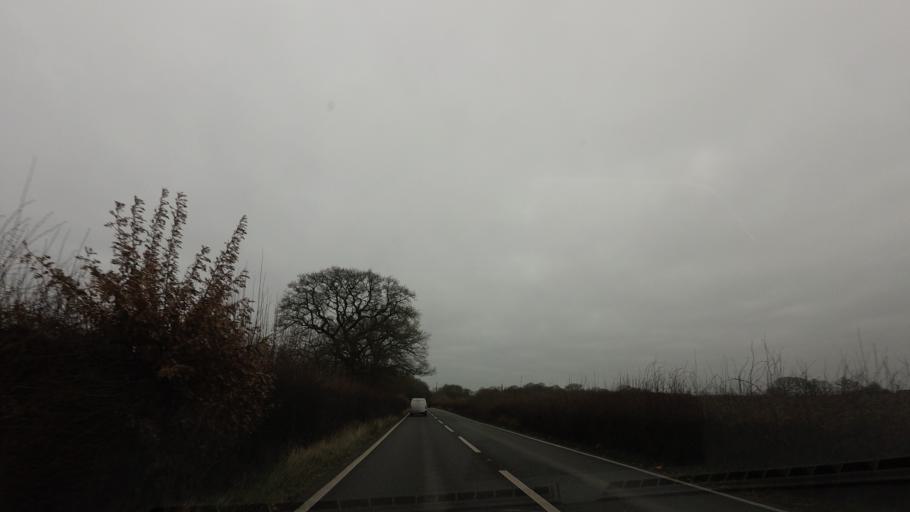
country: GB
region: England
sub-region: East Sussex
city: Saint Leonards-on-Sea
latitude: 50.9044
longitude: 0.5504
